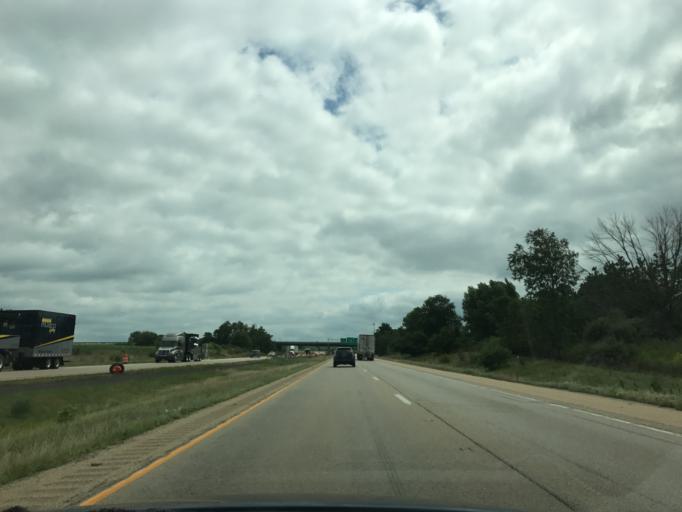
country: US
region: Illinois
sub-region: LaSalle County
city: La Salle
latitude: 41.3701
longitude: -89.0720
